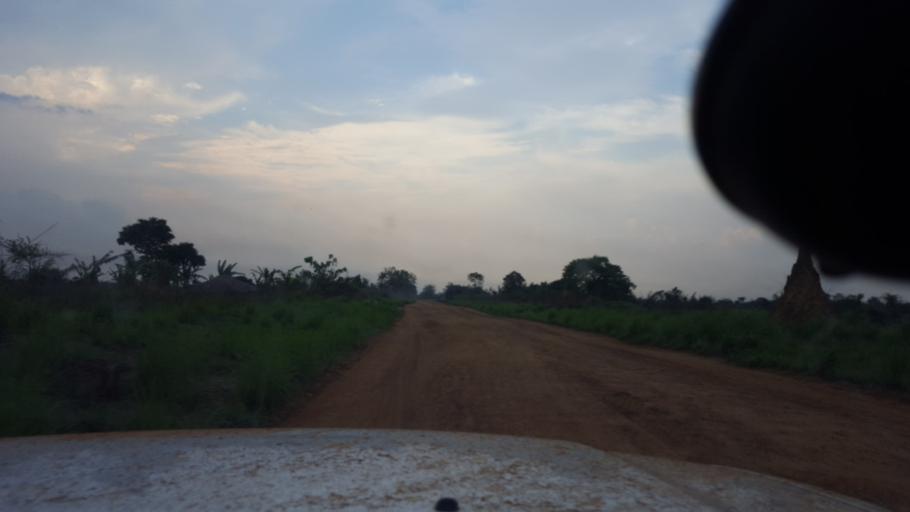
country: CD
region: Bandundu
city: Bandundu
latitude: -3.3797
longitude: 17.2597
